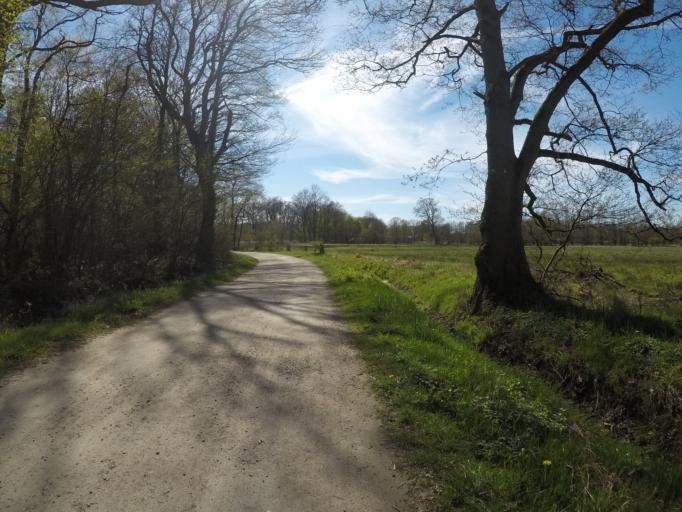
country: DE
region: Schleswig-Holstein
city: Jersbek
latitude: 53.7228
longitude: 10.1733
